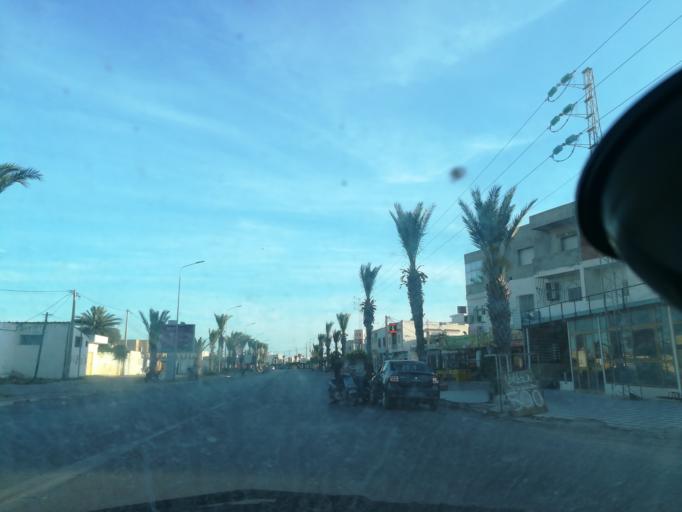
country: TN
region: Safaqis
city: Al Qarmadah
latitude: 34.8245
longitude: 10.7633
